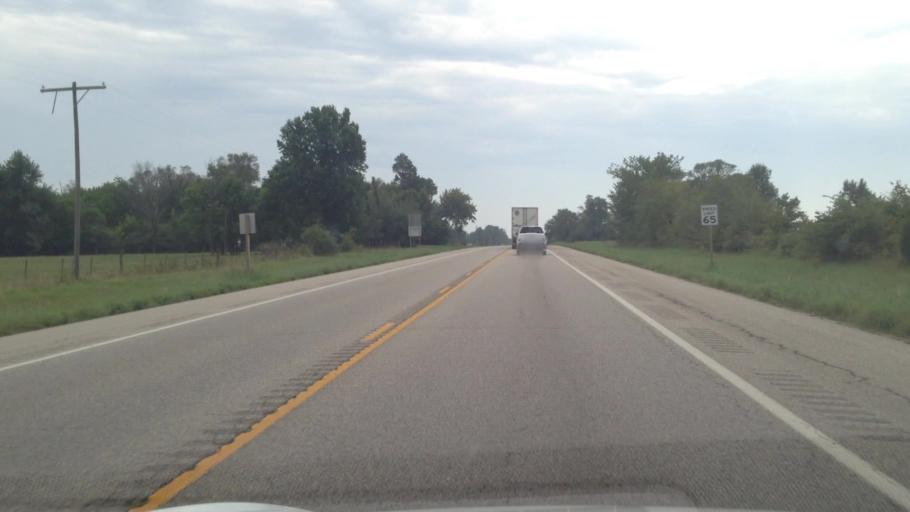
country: US
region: Kansas
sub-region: Crawford County
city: Pittsburg
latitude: 37.3292
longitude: -94.7054
